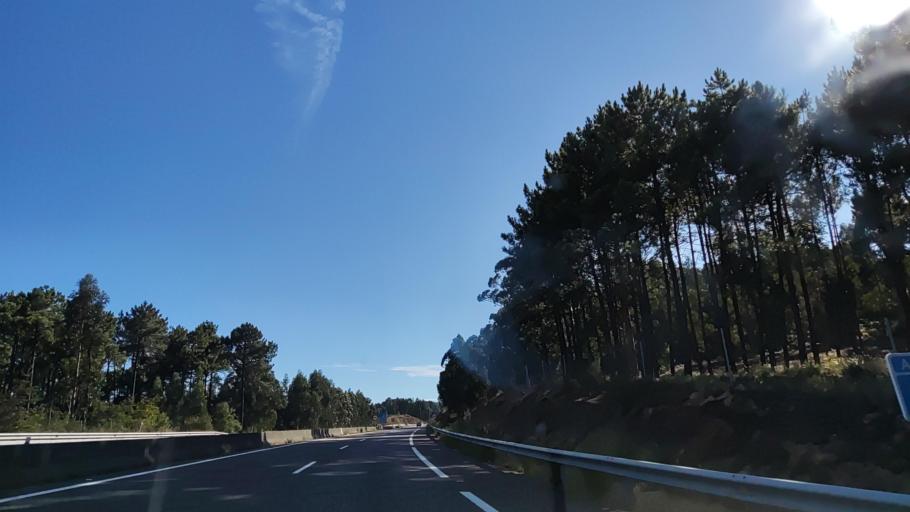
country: ES
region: Galicia
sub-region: Provincia da Coruna
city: Boiro
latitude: 42.5778
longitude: -8.9896
